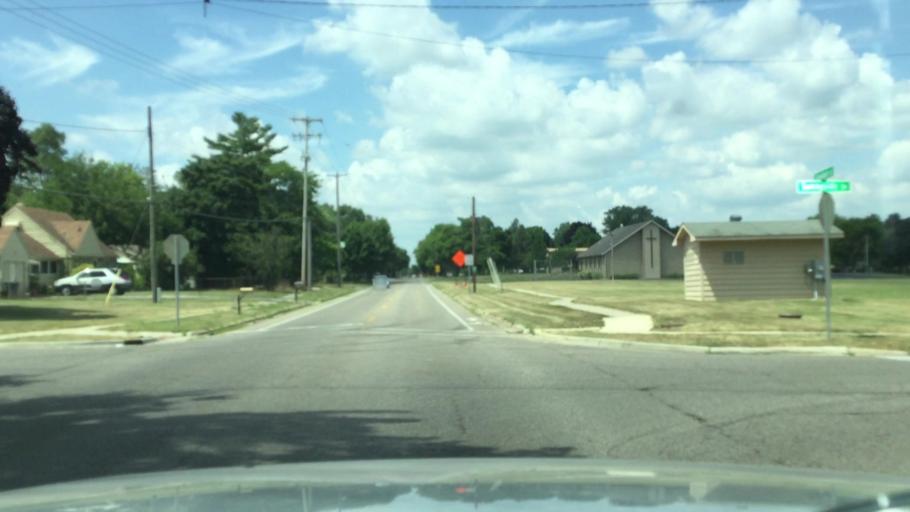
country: US
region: Michigan
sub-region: Genesee County
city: Flushing
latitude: 43.0674
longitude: -83.8253
